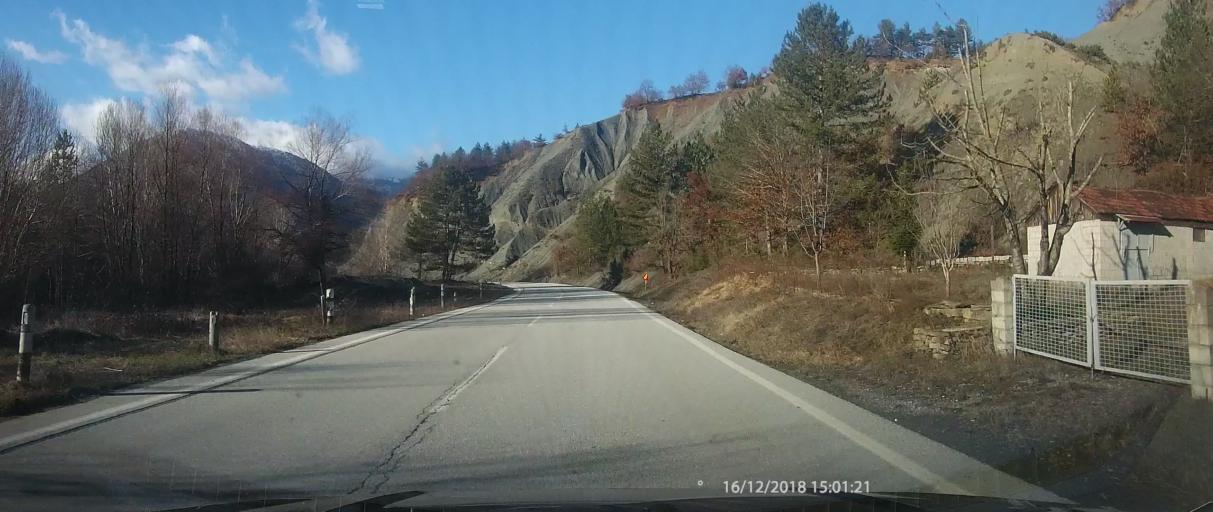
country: GR
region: West Macedonia
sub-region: Nomos Kastorias
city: Nestorio
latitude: 40.2208
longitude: 21.0070
